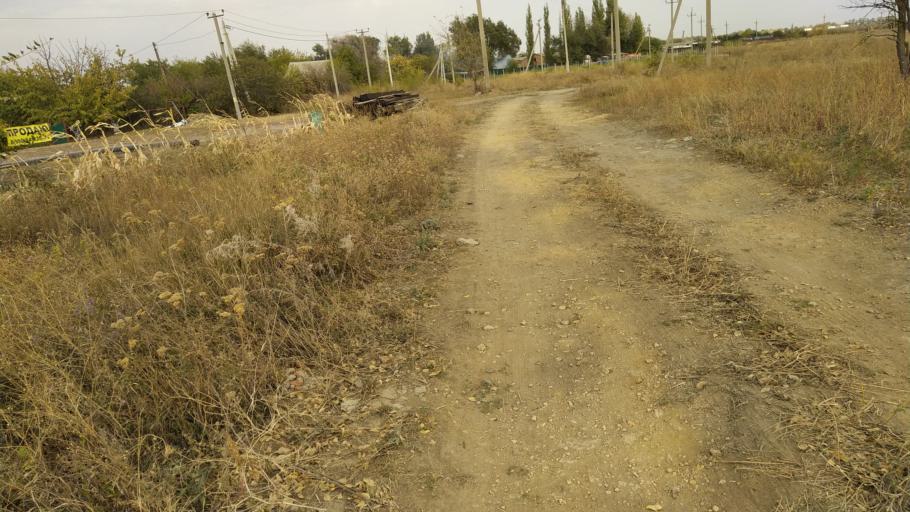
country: RU
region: Rostov
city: Kuleshovka
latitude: 47.1088
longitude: 39.6155
